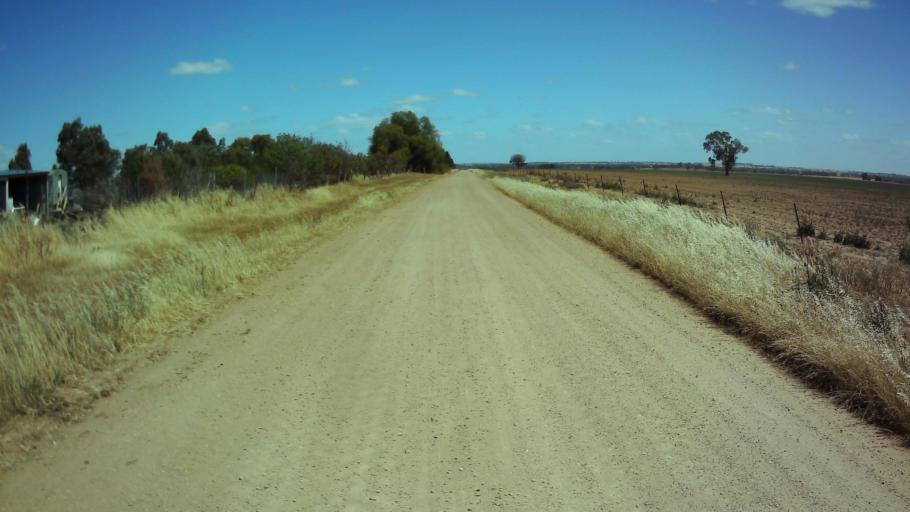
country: AU
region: New South Wales
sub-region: Weddin
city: Grenfell
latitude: -33.9716
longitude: 148.3278
